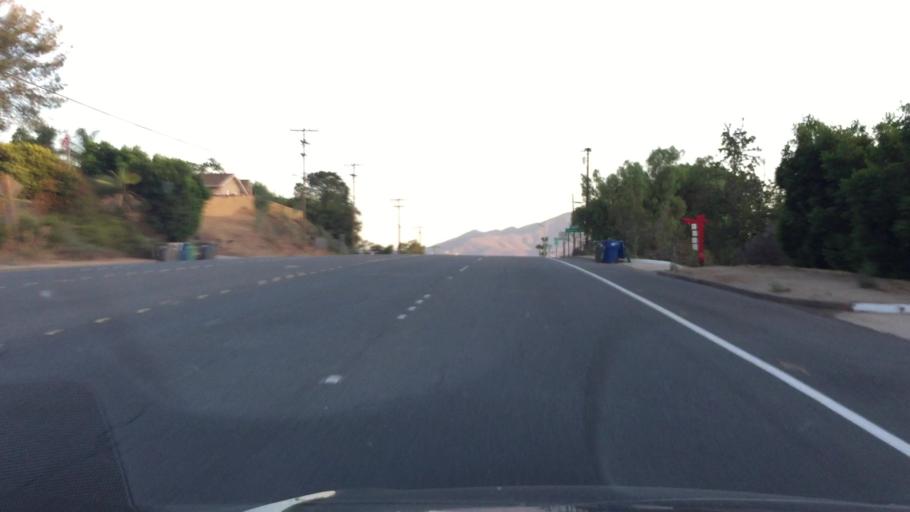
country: US
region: California
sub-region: San Diego County
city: Rancho San Diego
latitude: 32.7771
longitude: -116.9280
